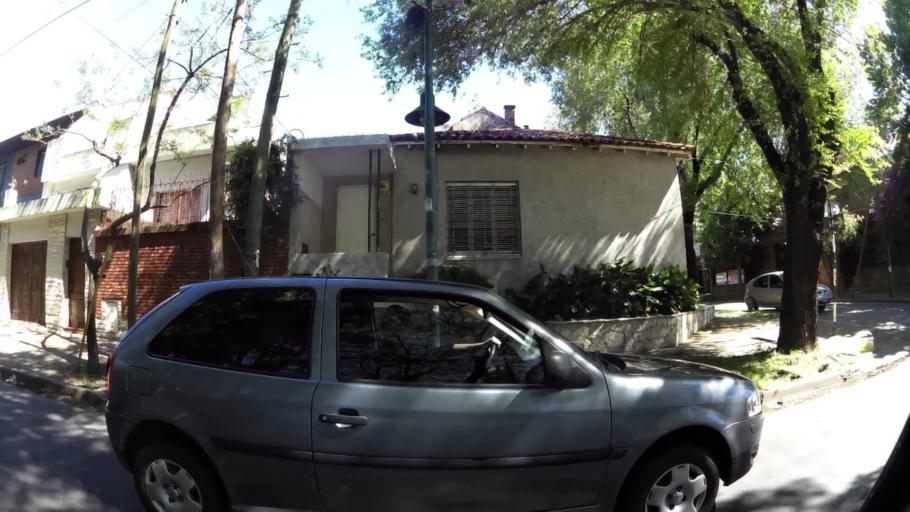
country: AR
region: Buenos Aires
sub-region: Partido de Vicente Lopez
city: Olivos
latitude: -34.5249
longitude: -58.4998
